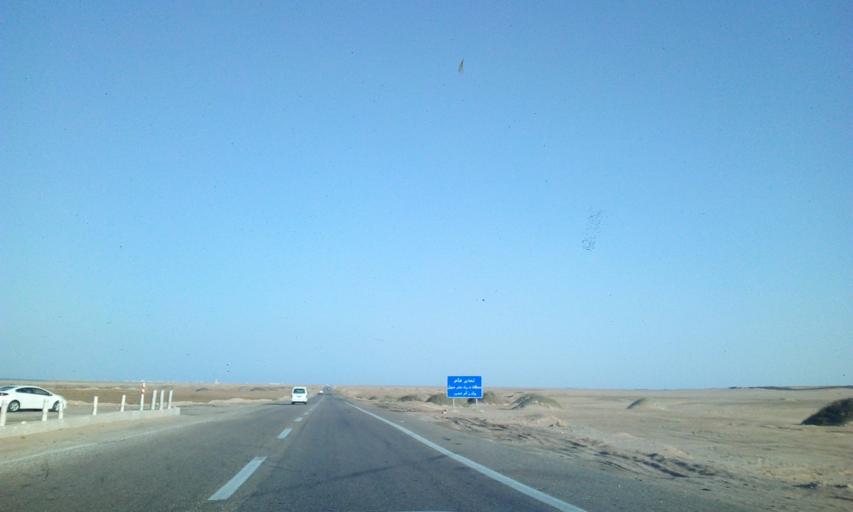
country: EG
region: South Sinai
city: Tor
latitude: 28.5672
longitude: 32.8687
